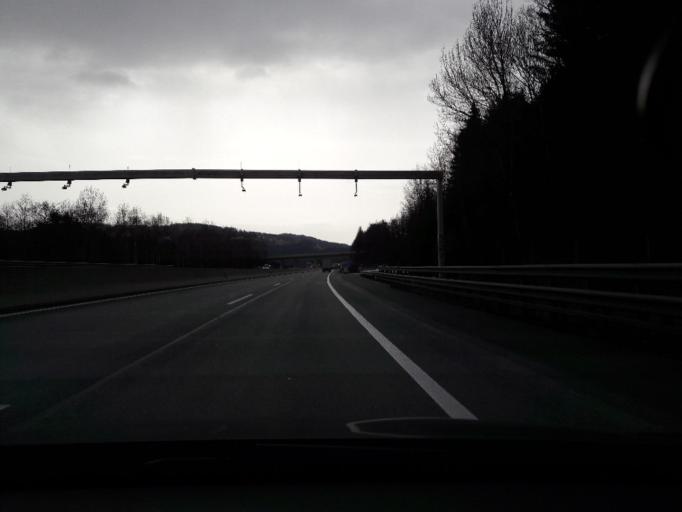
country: AT
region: Styria
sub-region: Politischer Bezirk Hartberg-Fuerstenfeld
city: Schaeffern
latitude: 47.4497
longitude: 16.0979
